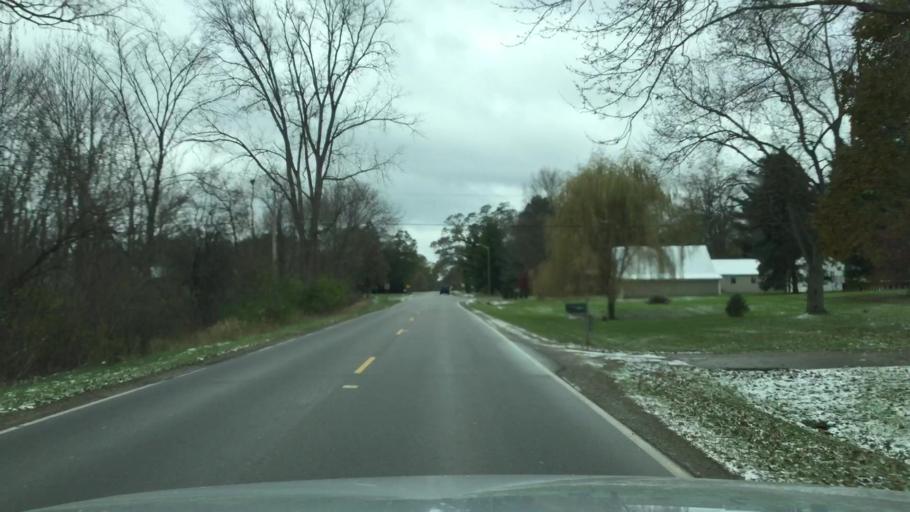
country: US
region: Michigan
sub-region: Livingston County
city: Brighton
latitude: 42.5384
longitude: -83.7290
